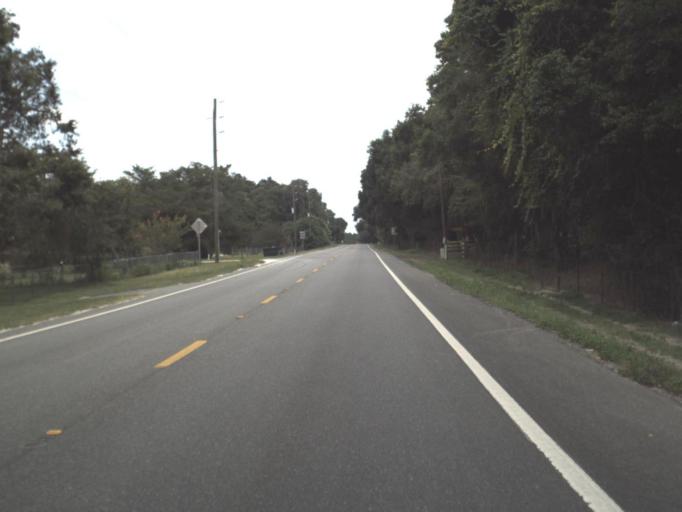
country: US
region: Florida
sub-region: Pasco County
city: Lacoochee
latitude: 28.4680
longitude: -82.1664
